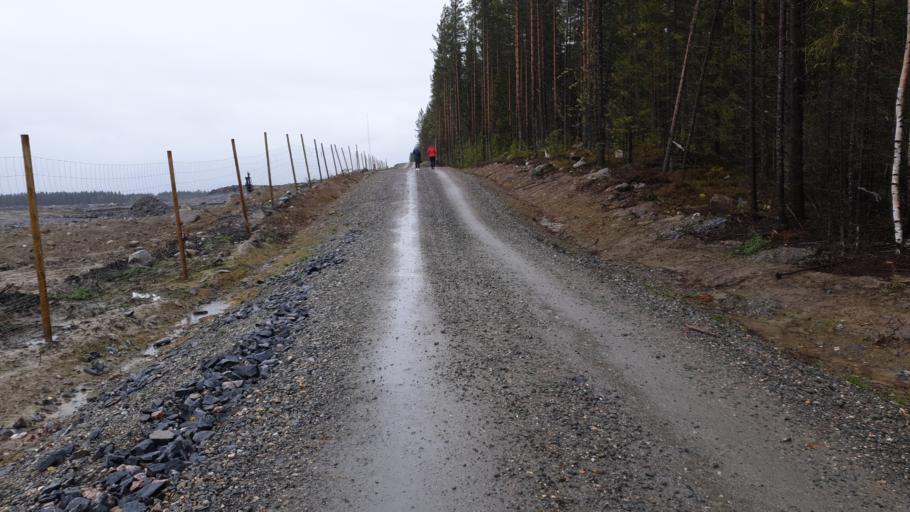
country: SE
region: Vaesterbotten
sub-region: Skelleftea Kommun
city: Soedra Bergsbyn
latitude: 64.7405
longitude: 21.0760
